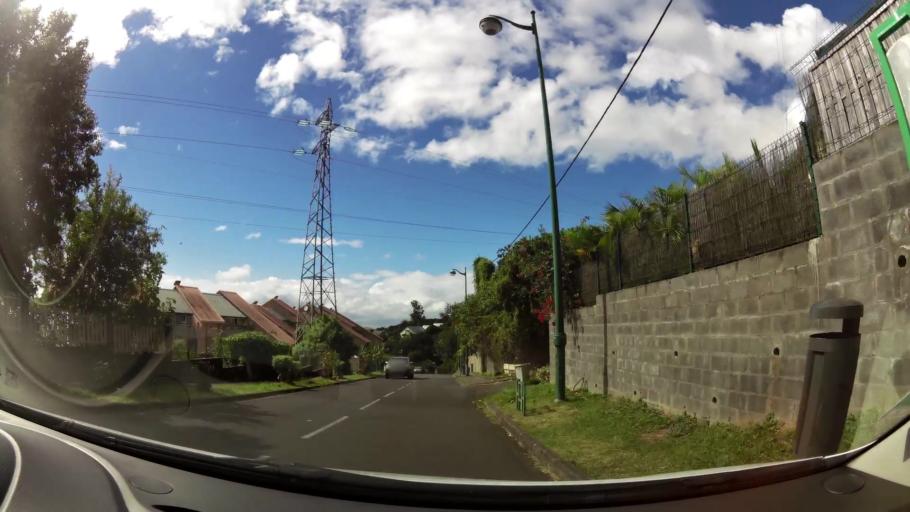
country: RE
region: Reunion
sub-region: Reunion
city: Saint-Denis
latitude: -20.9265
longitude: 55.4875
